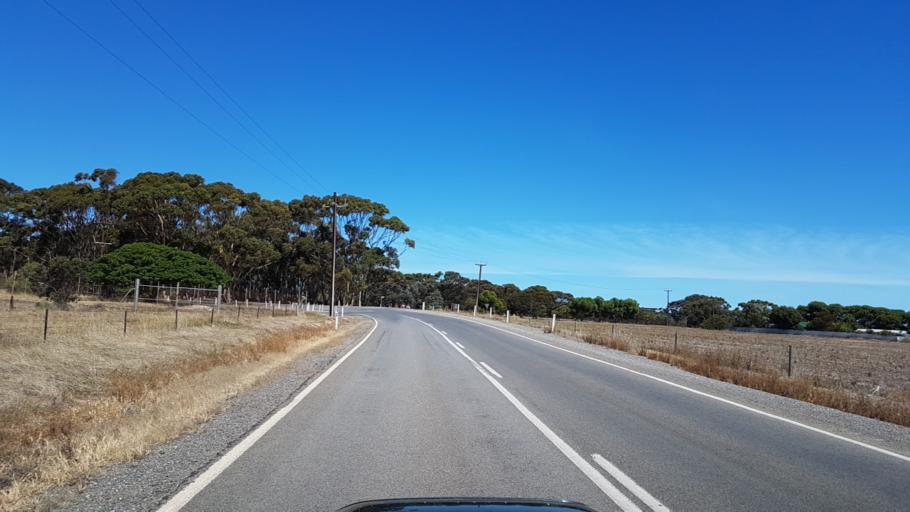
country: AU
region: South Australia
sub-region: Yorke Peninsula
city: Maitland
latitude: -34.3675
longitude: 137.6695
